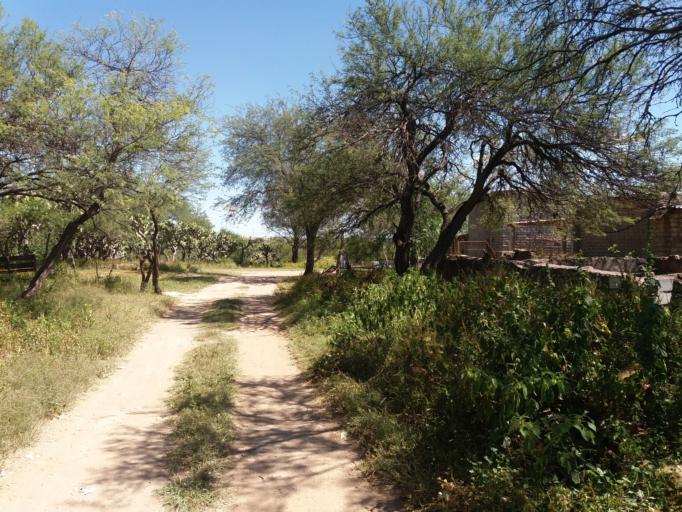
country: MX
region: Aguascalientes
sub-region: Aguascalientes
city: Villa Licenciado Jesus Teran (Calvillito)
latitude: 21.7841
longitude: -102.2263
